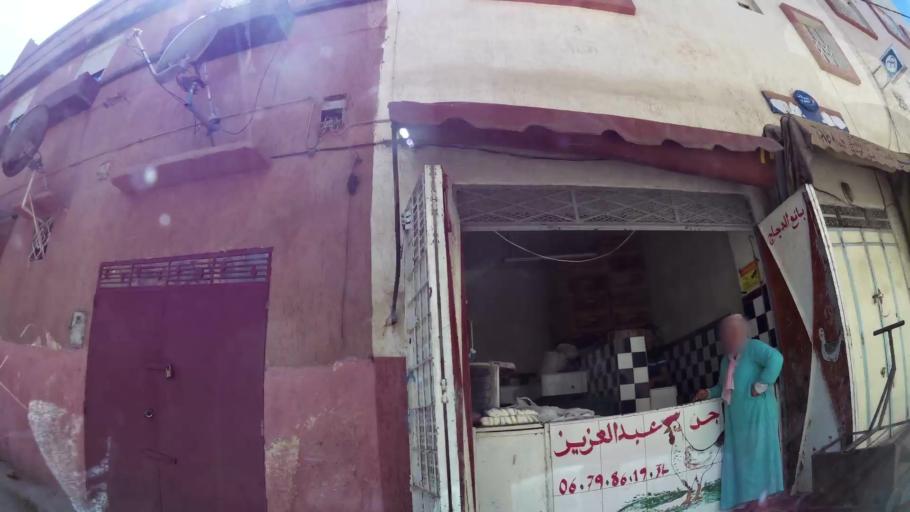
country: MA
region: Meknes-Tafilalet
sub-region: Meknes
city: Meknes
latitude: 33.8712
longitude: -5.5627
